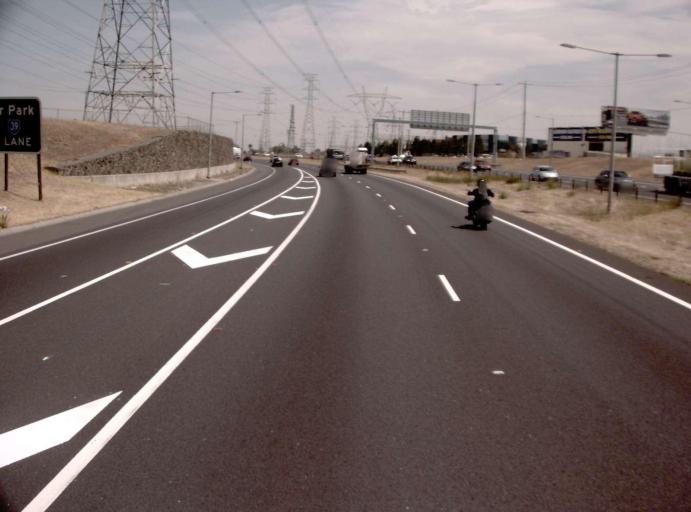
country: AU
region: Victoria
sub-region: Moonee Valley
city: Keilor East
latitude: -37.7312
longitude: 144.8554
